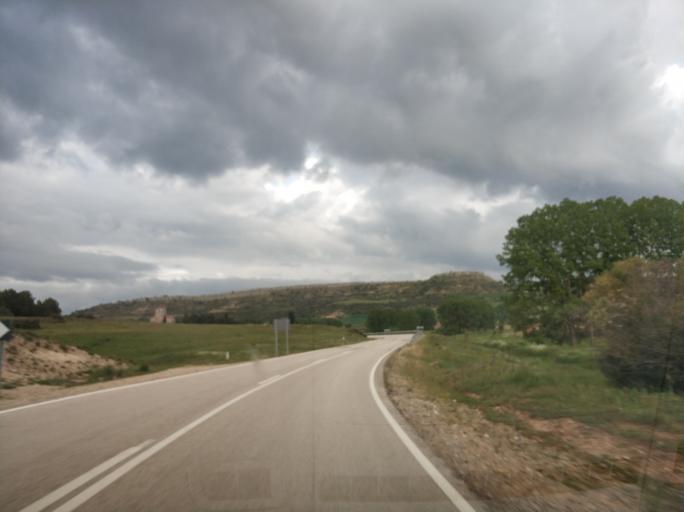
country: ES
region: Castille and Leon
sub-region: Provincia de Soria
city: Santa Maria de las Hoyas
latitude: 41.7690
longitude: -3.1495
